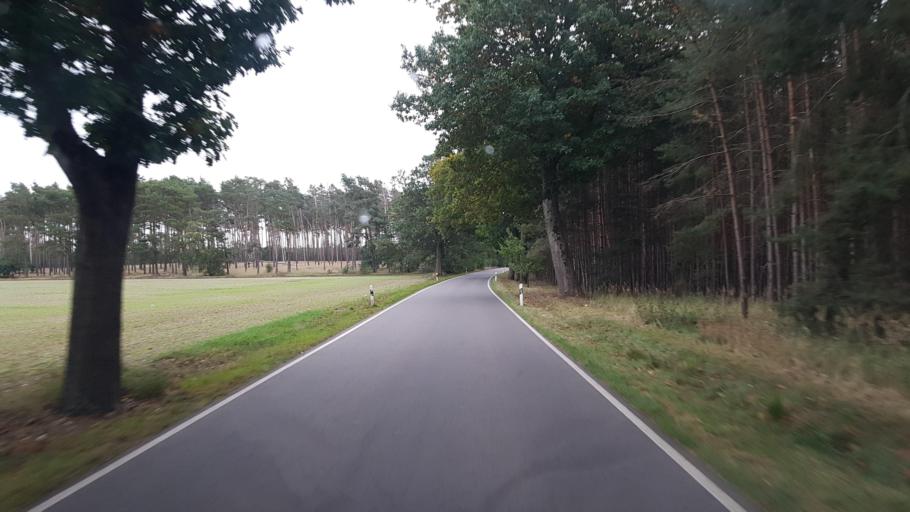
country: DE
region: Brandenburg
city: Kasel-Golzig
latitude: 51.8899
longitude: 13.6565
